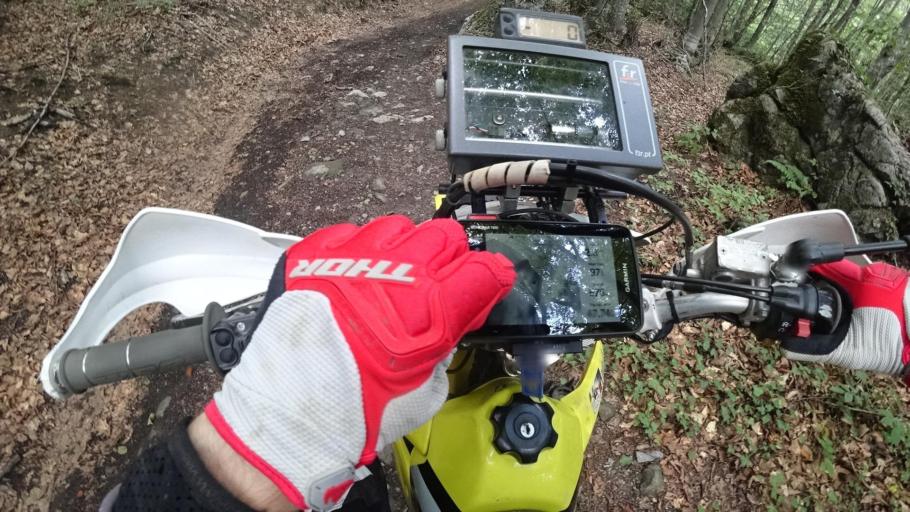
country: HR
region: Karlovacka
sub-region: Grad Ogulin
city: Ogulin
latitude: 45.2298
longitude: 15.1844
